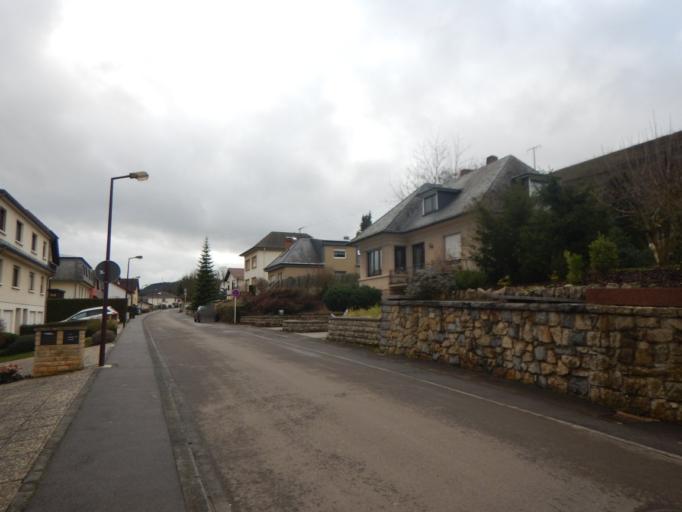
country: LU
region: Grevenmacher
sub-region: Canton de Grevenmacher
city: Grevenmacher
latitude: 49.6755
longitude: 6.4357
